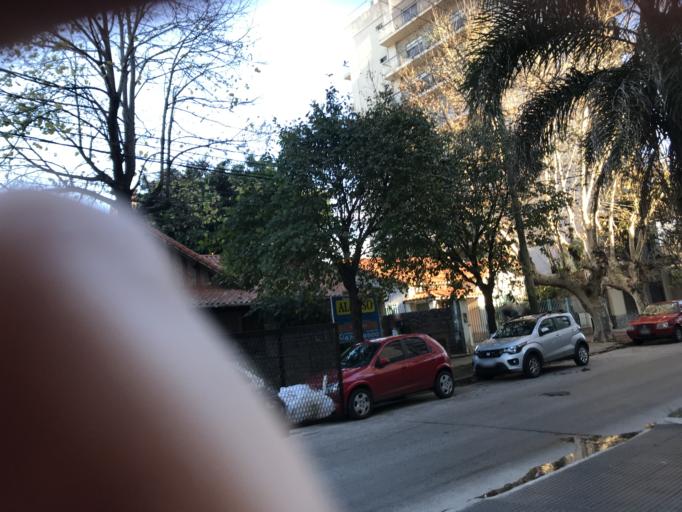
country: AR
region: Buenos Aires
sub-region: Partido de General San Martin
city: General San Martin
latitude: -34.5513
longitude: -58.5511
